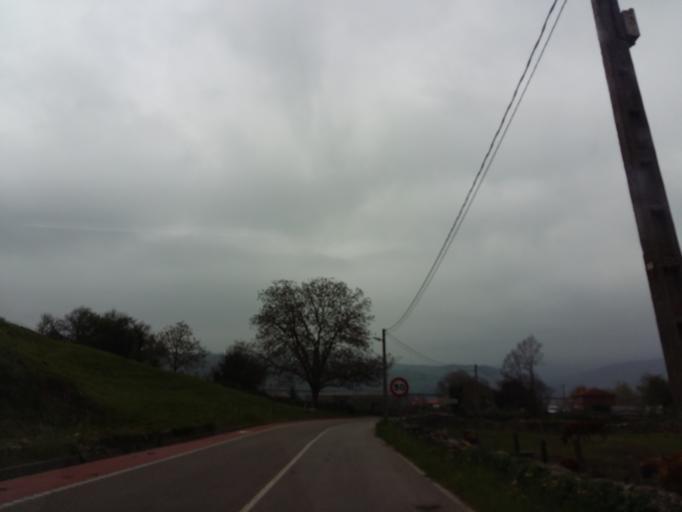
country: ES
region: Cantabria
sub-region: Provincia de Cantabria
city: Arenas de Iguna
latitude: 43.1909
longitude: -4.0815
